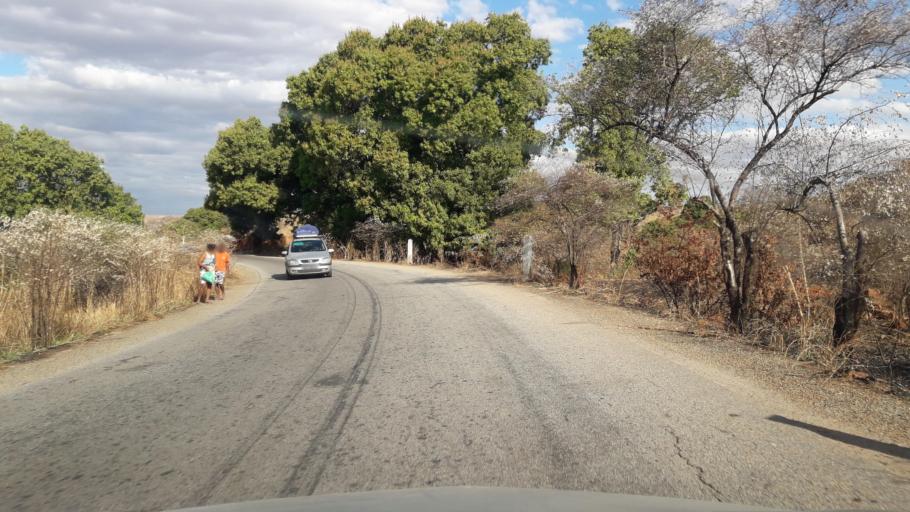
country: MG
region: Betsiboka
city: Maevatanana
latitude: -17.2771
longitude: 46.9440
